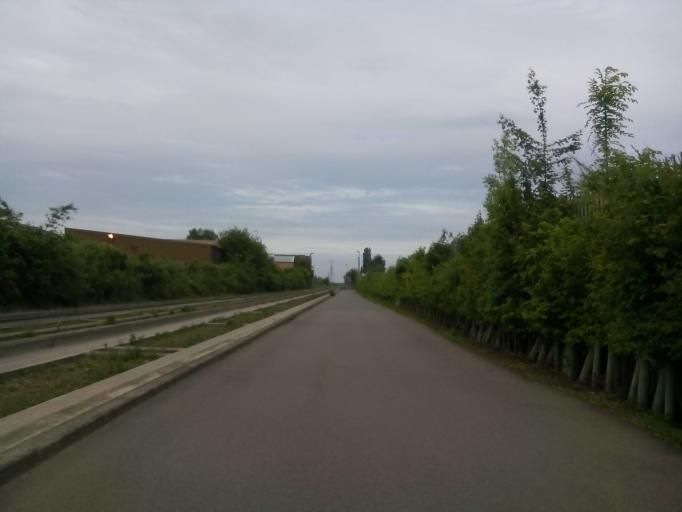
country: GB
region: England
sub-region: Cambridgeshire
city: Swavesey
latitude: 52.2925
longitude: 0.0520
